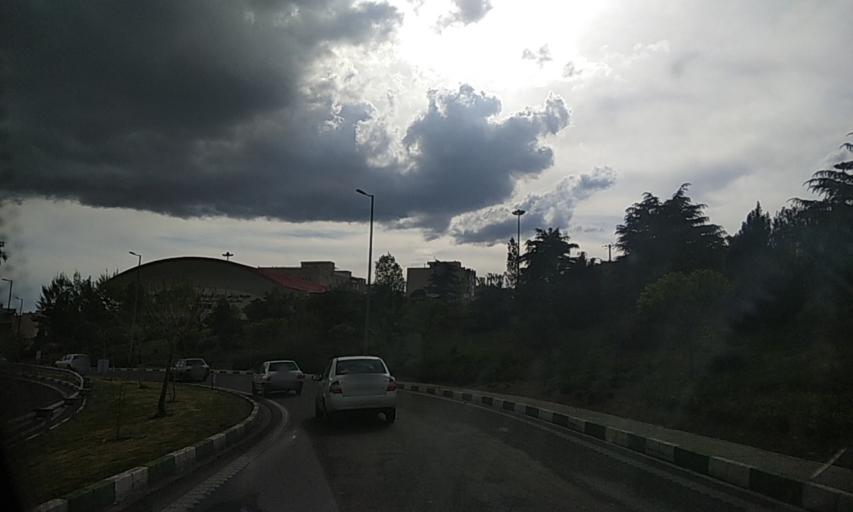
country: IR
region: Tehran
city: Tajrish
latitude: 35.7547
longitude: 51.2941
